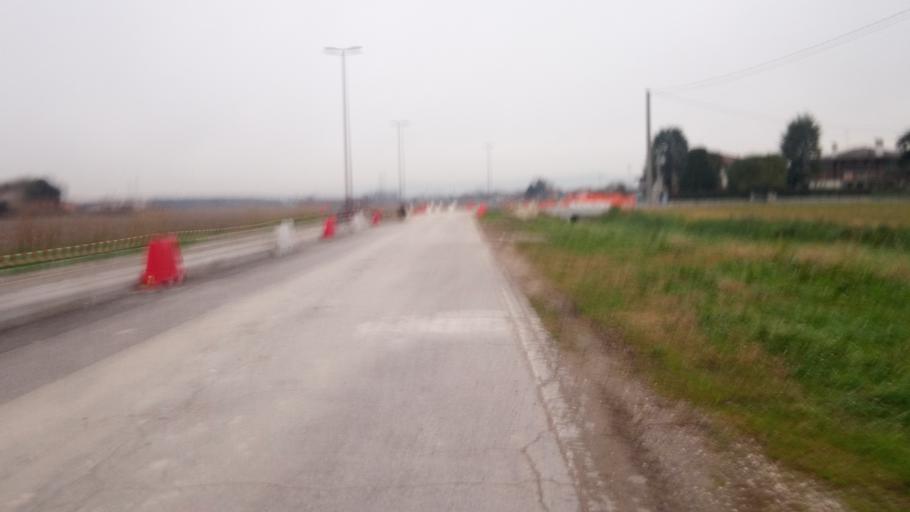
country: IT
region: Veneto
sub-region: Provincia di Padova
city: Sarmeola
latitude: 45.4275
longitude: 11.8191
